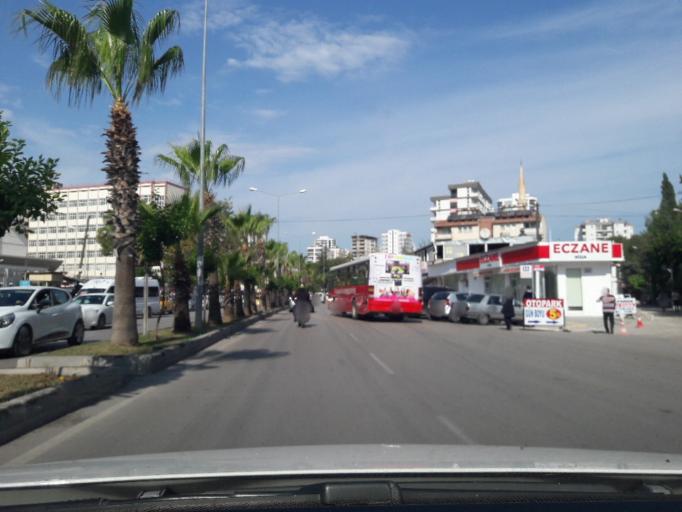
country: TR
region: Adana
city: Adana
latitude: 37.0192
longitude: 35.3207
